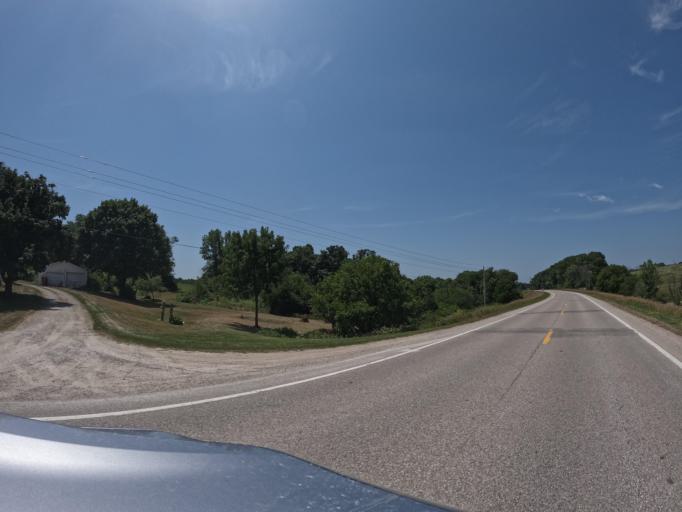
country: US
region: Iowa
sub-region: Henry County
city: Mount Pleasant
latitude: 40.9379
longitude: -91.5931
